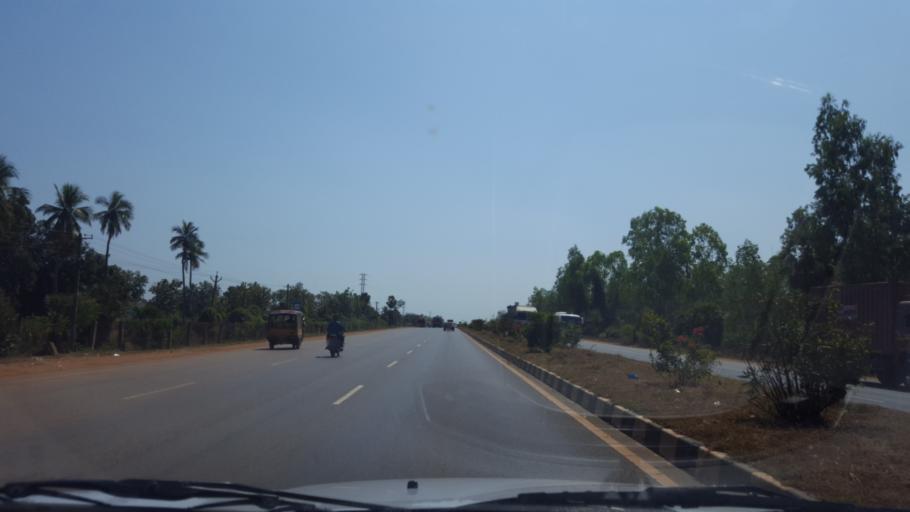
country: IN
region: Andhra Pradesh
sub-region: Nellore
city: Kavali
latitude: 14.8023
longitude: 79.9965
